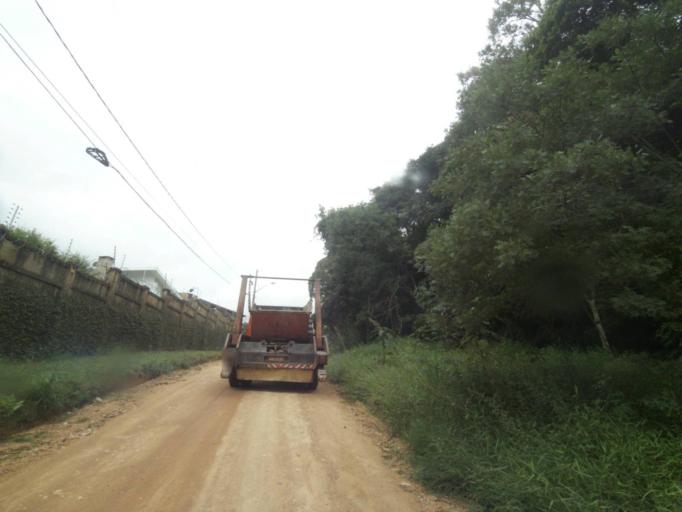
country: BR
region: Parana
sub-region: Curitiba
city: Curitiba
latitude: -25.4566
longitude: -49.3387
